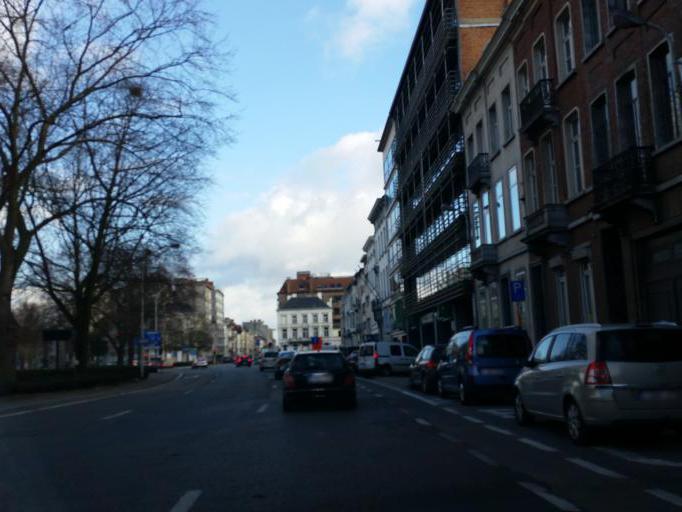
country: BE
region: Flanders
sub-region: Provincie Antwerpen
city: Mechelen
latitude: 51.0214
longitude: 4.4744
